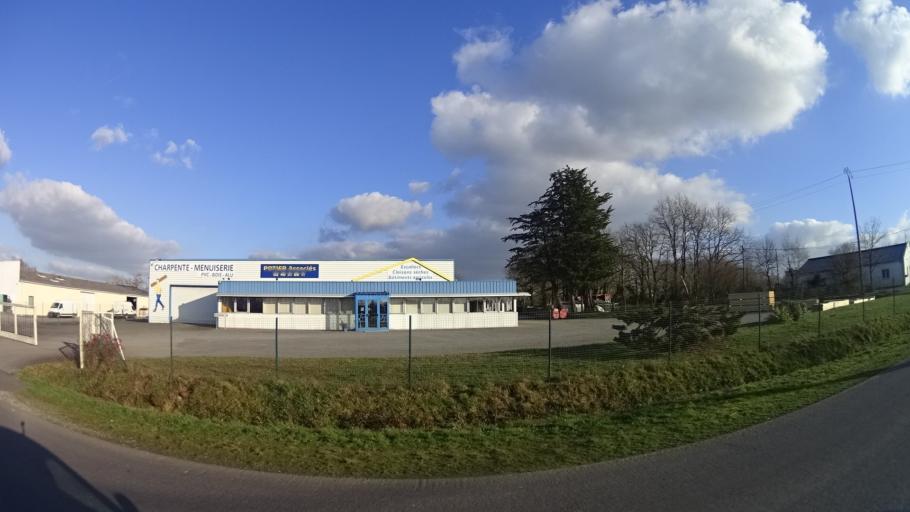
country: FR
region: Pays de la Loire
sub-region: Departement de la Loire-Atlantique
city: Plesse
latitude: 47.5273
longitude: -1.8863
